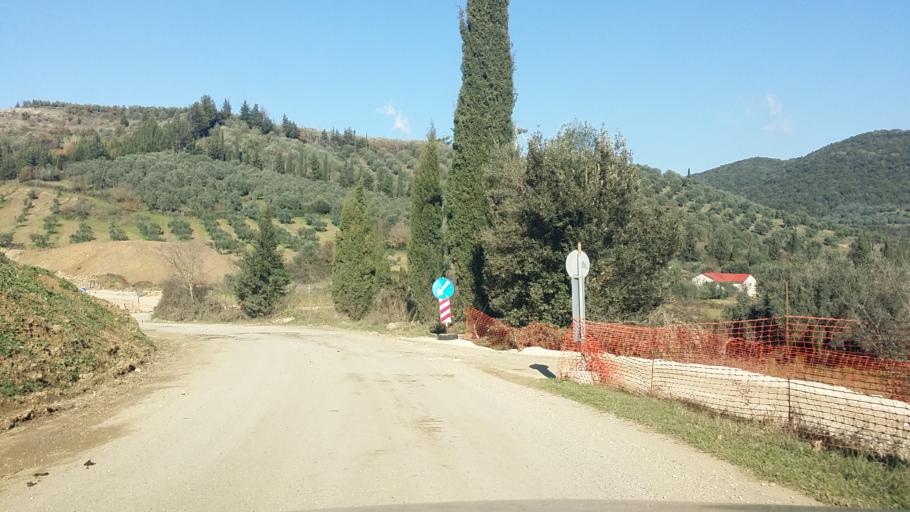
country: GR
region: West Greece
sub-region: Nomos Aitolias kai Akarnanias
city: Krikellos
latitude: 38.9575
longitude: 21.1874
